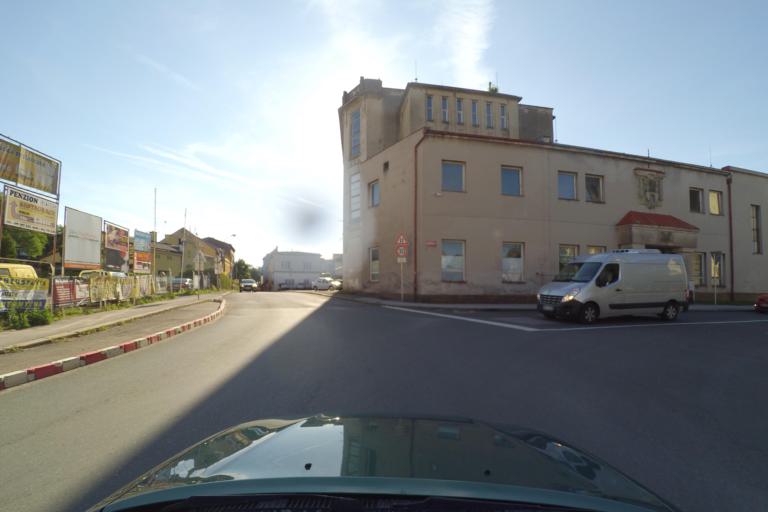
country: CZ
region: Kralovehradecky
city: Dvur Kralove nad Labem
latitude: 50.4344
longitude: 15.8137
